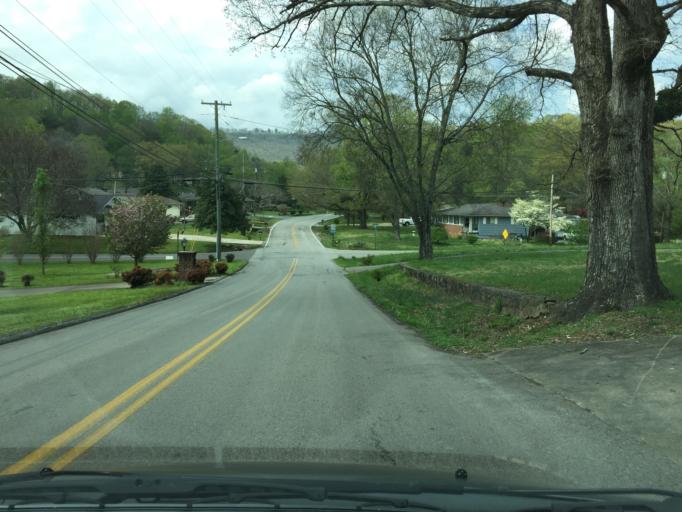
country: US
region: Tennessee
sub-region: Hamilton County
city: Red Bank
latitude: 35.1385
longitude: -85.2832
